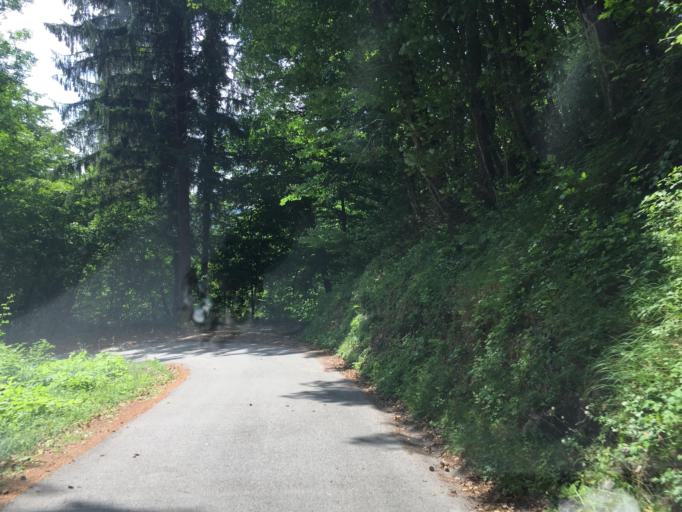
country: SI
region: Tolmin
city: Tolmin
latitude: 46.1626
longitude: 13.8369
